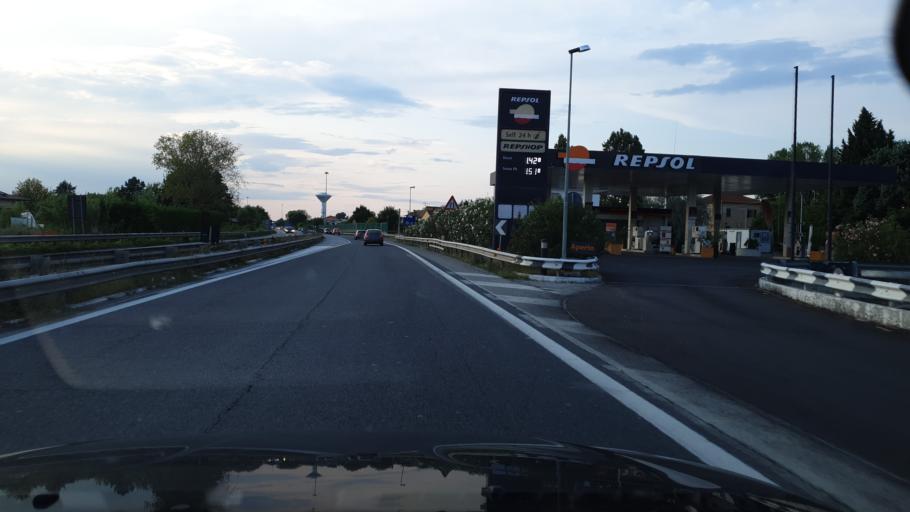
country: IT
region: Emilia-Romagna
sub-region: Forli-Cesena
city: Cesenatico
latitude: 44.1870
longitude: 12.4074
